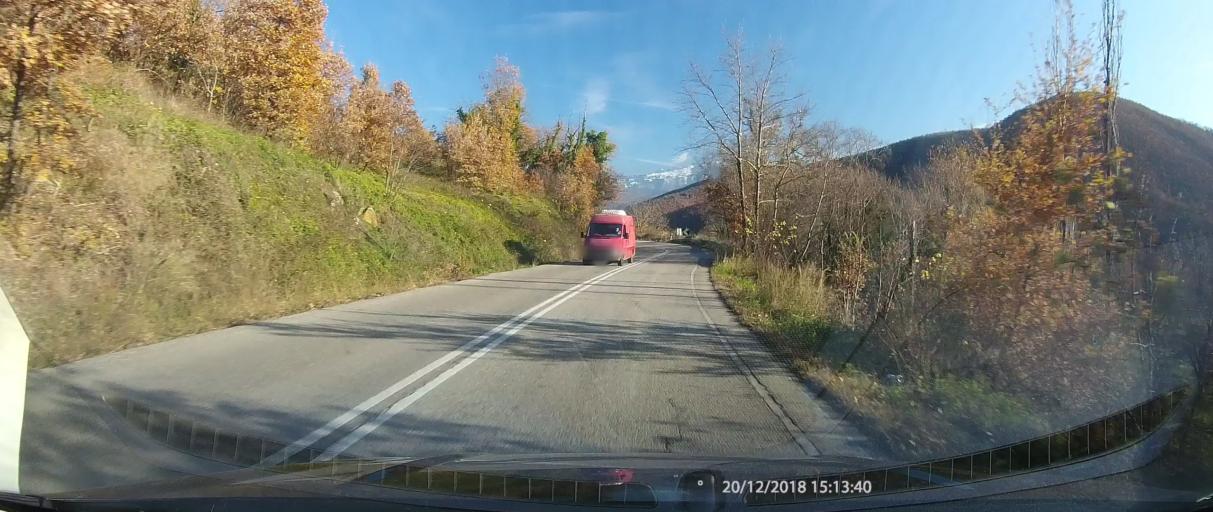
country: GR
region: Central Greece
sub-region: Nomos Fthiotidos
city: Makrakomi
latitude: 38.9322
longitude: 21.9707
